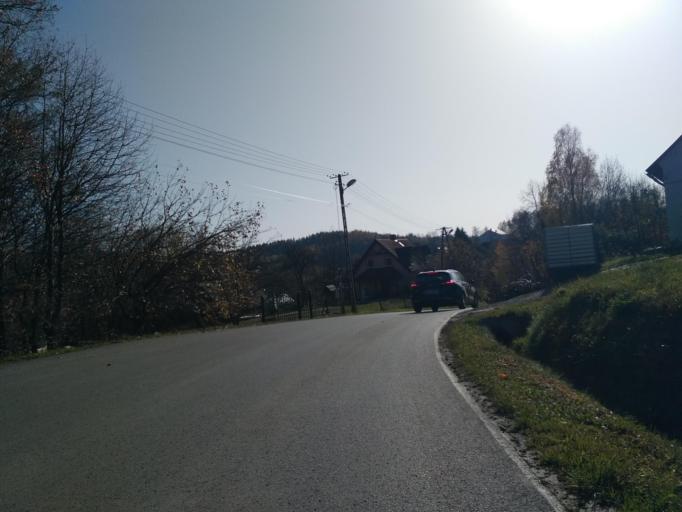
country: PL
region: Subcarpathian Voivodeship
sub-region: Powiat brzozowski
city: Nozdrzec
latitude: 49.8164
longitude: 22.1665
